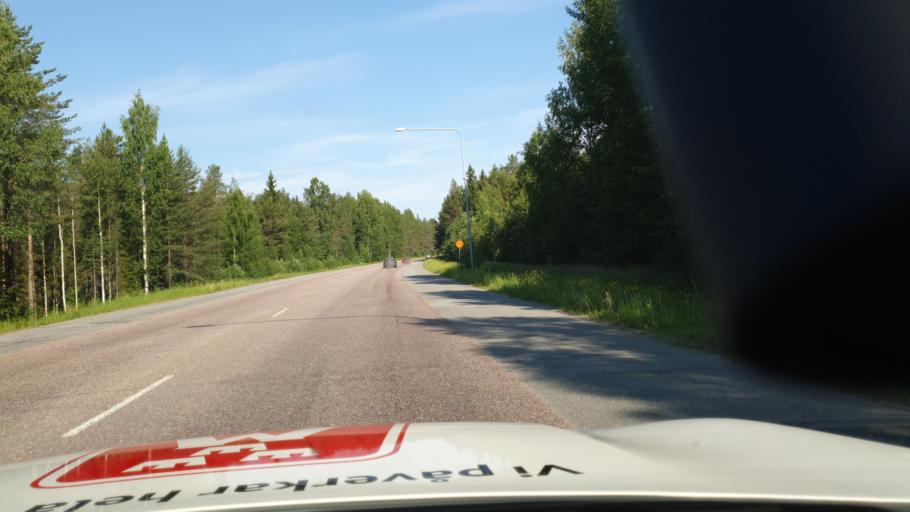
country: SE
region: Vaesterbotten
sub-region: Skelleftea Kommun
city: Skelleftea
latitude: 64.7561
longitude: 21.0123
